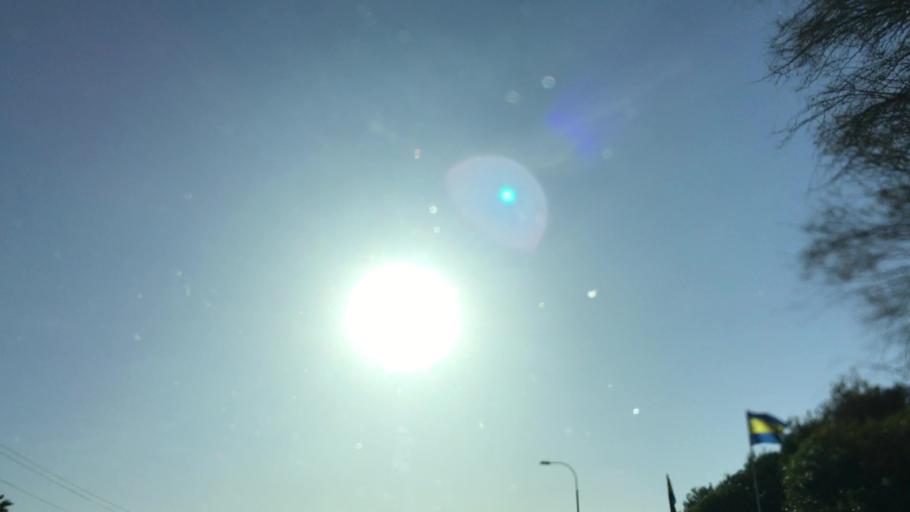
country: US
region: Arizona
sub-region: Maricopa County
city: Peoria
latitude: 33.5817
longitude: -112.2081
